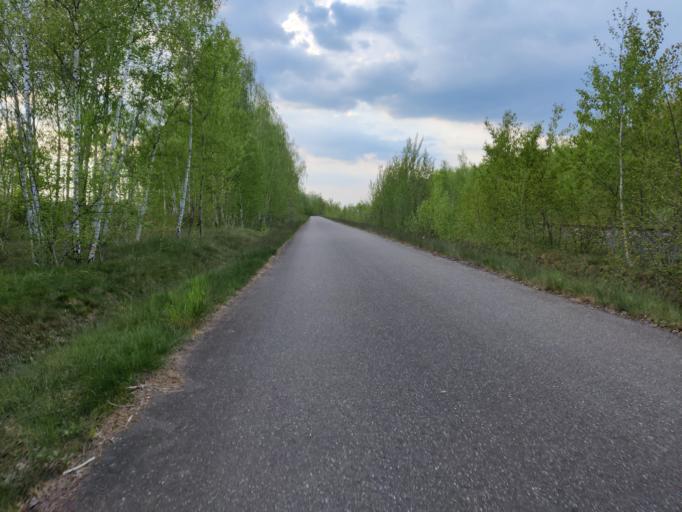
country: DE
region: Saxony
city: Rotha
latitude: 51.2159
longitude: 12.4304
